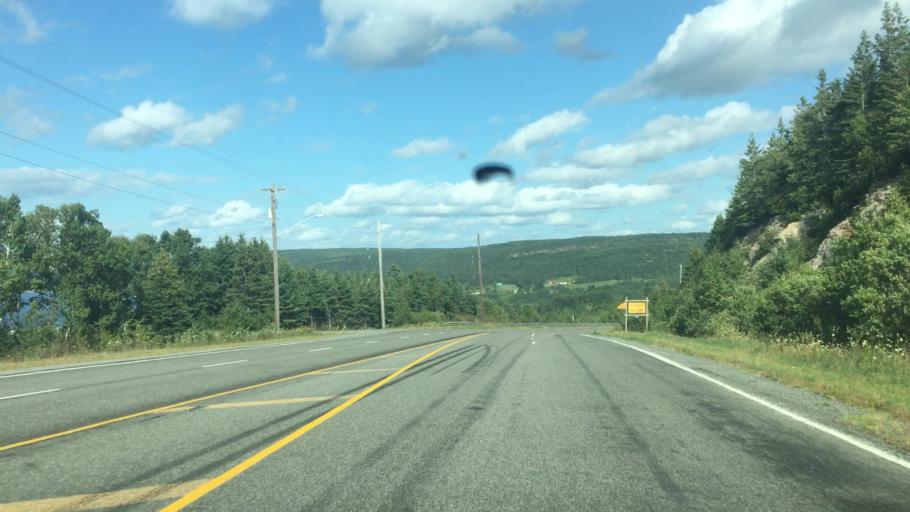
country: CA
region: Nova Scotia
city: Sydney
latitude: 45.8151
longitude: -60.6918
